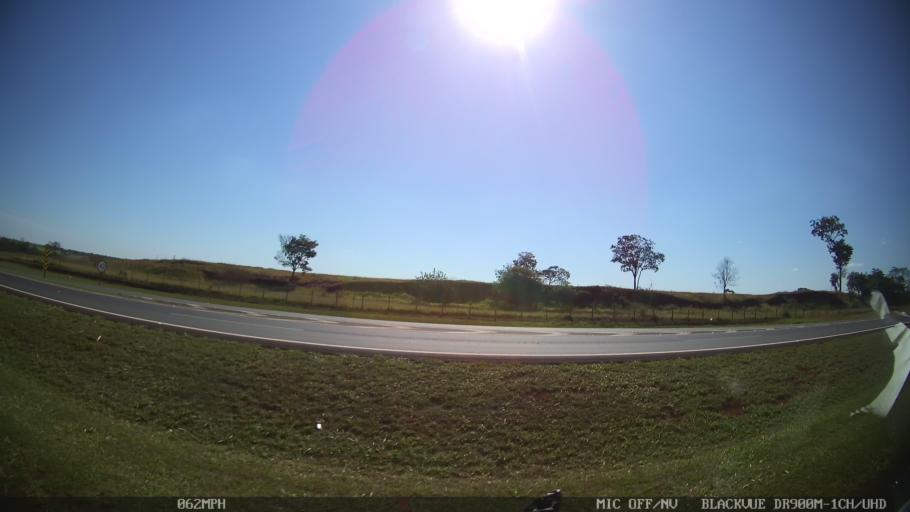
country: BR
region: Sao Paulo
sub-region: Ribeirao Preto
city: Ribeirao Preto
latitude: -21.1049
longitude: -47.8071
